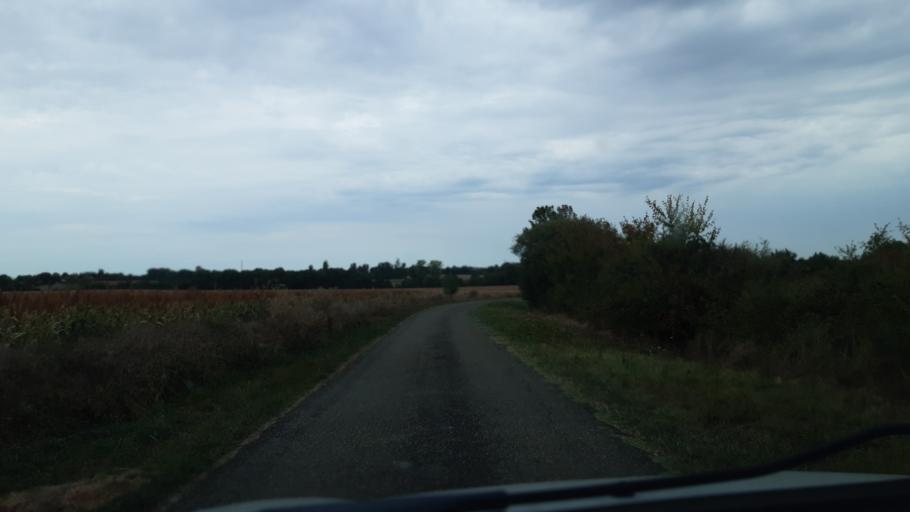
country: FR
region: Midi-Pyrenees
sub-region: Departement du Gers
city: Gimont
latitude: 43.6588
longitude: 0.9820
